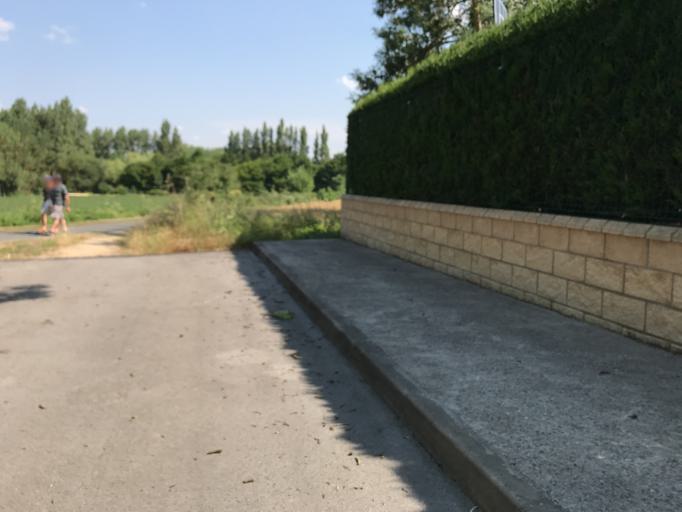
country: ES
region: Basque Country
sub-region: Provincia de Alava
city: Gasteiz / Vitoria
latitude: 42.8833
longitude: -2.6465
